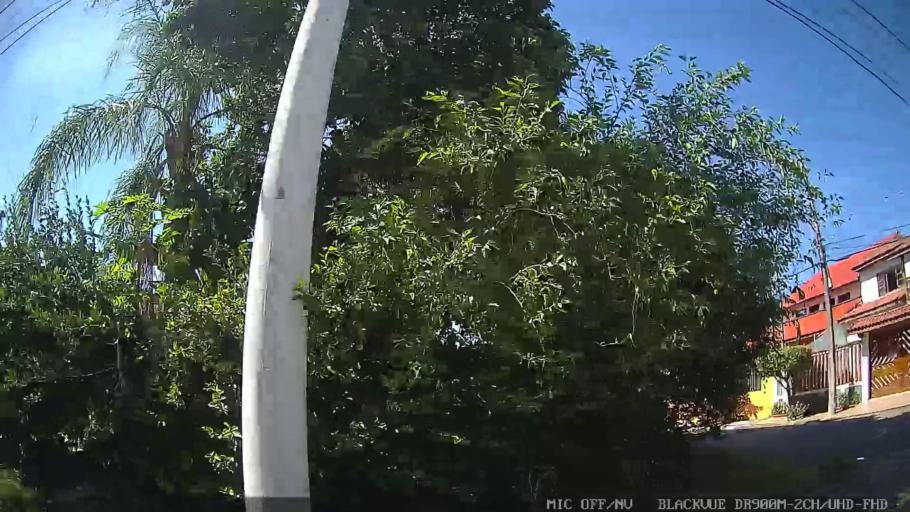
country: BR
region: Sao Paulo
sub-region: Peruibe
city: Peruibe
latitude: -24.2764
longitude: -46.9420
